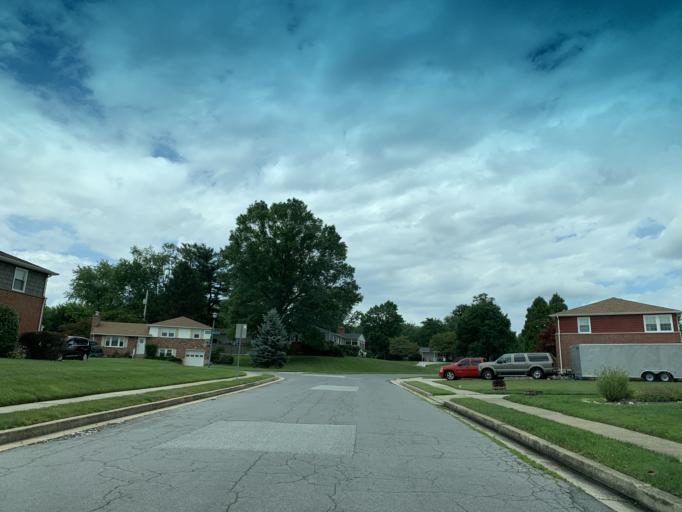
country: US
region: Maryland
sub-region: Baltimore County
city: Timonium
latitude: 39.4433
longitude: -76.6148
